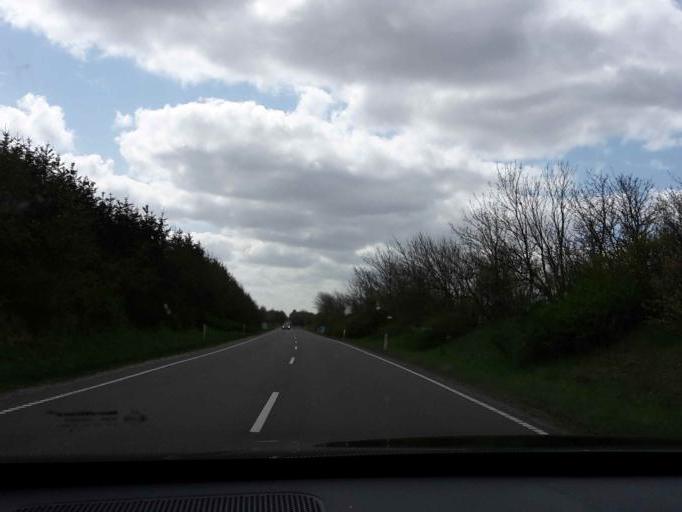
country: DK
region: South Denmark
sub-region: Varde Kommune
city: Olgod
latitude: 55.7075
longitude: 8.6080
